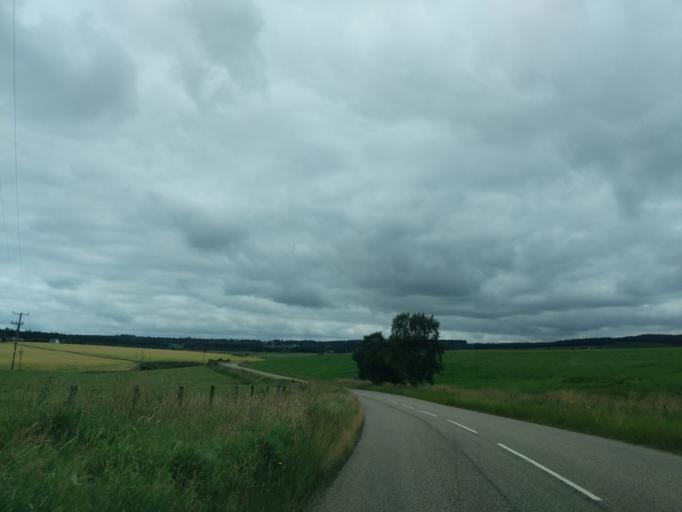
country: GB
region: Scotland
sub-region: Moray
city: Rothes
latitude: 57.4917
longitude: -3.2189
